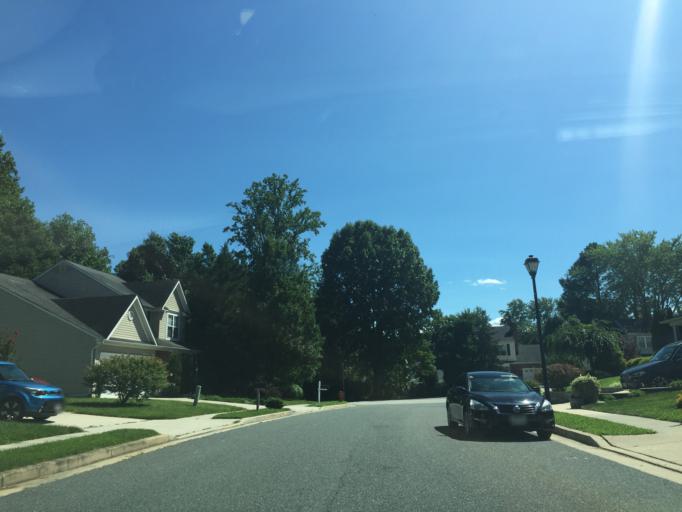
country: US
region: Maryland
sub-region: Baltimore County
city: Perry Hall
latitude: 39.4136
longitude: -76.4800
